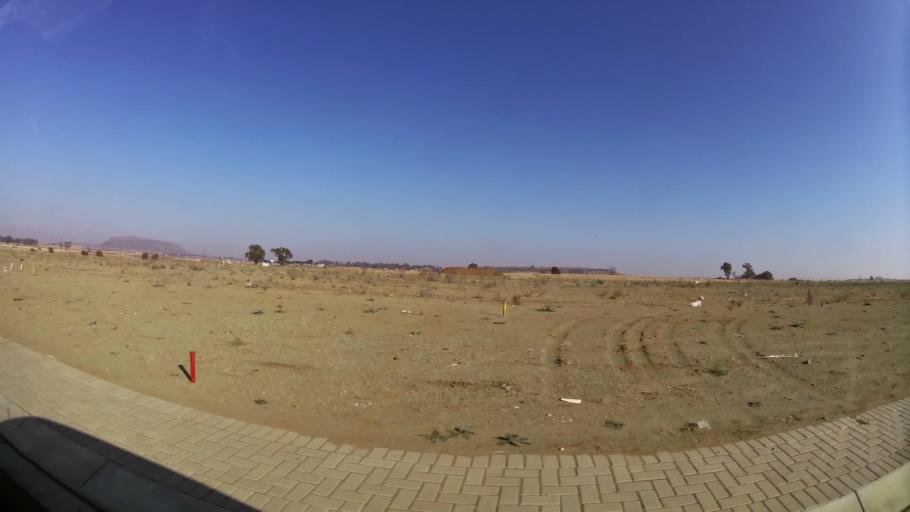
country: ZA
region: Orange Free State
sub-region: Mangaung Metropolitan Municipality
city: Bloemfontein
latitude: -29.1998
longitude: 26.2172
